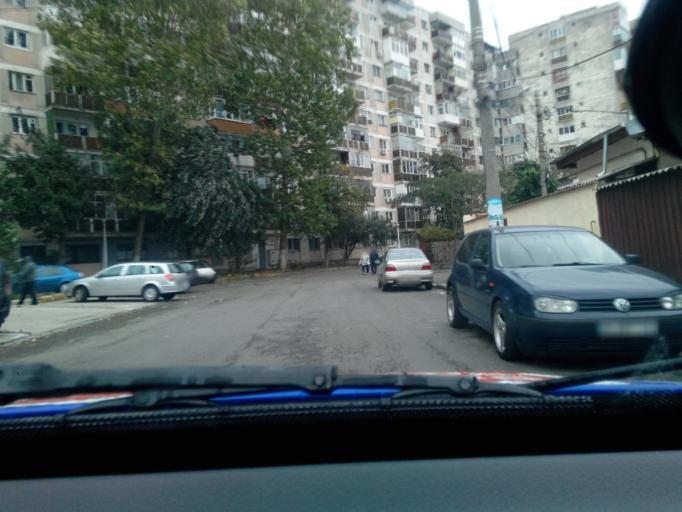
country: RO
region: Bucuresti
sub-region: Municipiul Bucuresti
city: Bucuresti
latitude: 44.4040
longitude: 26.0571
